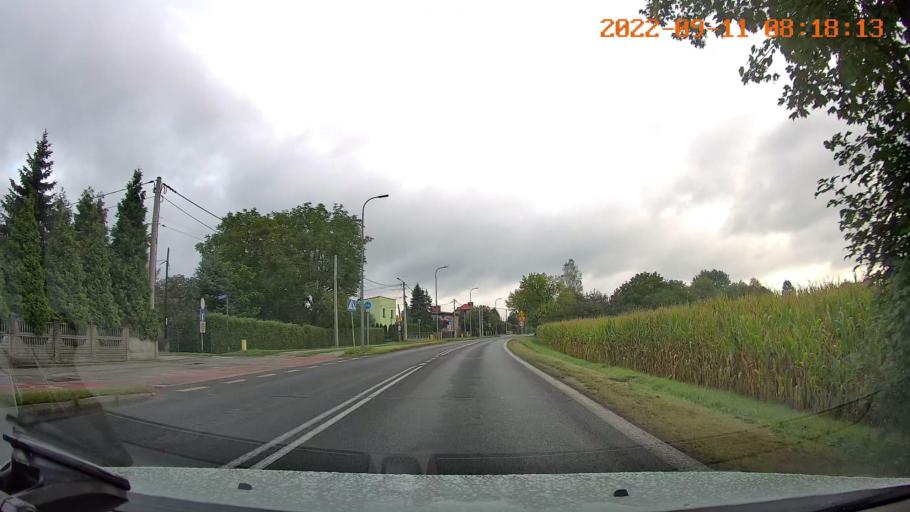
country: PL
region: Silesian Voivodeship
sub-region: Tychy
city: Tychy
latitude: 50.1439
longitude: 18.9970
